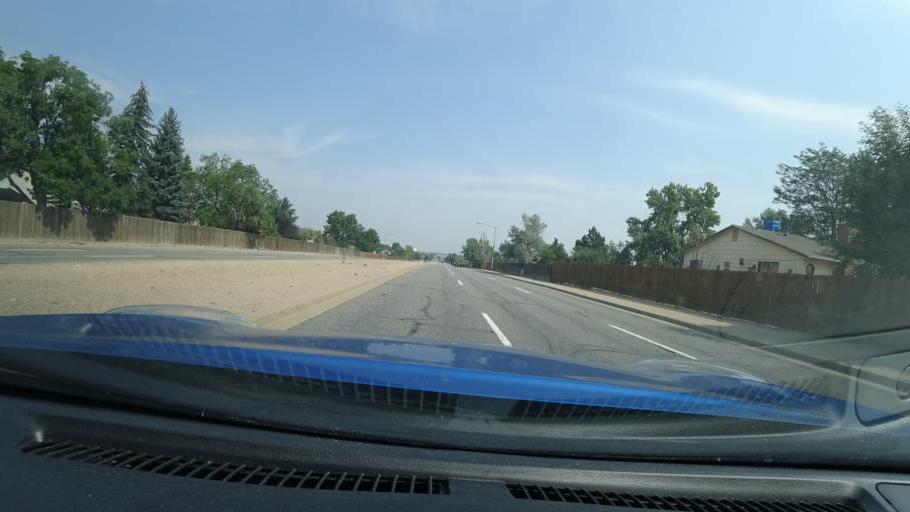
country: US
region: Colorado
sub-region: Adams County
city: Aurora
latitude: 39.6892
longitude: -104.7723
